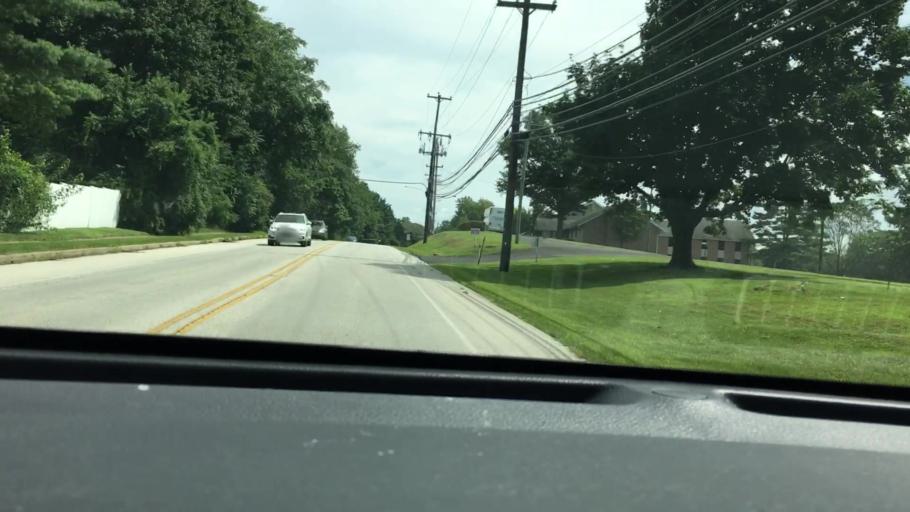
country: US
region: Pennsylvania
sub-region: Montgomery County
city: Bryn Athyn
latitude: 40.1505
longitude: -75.0604
